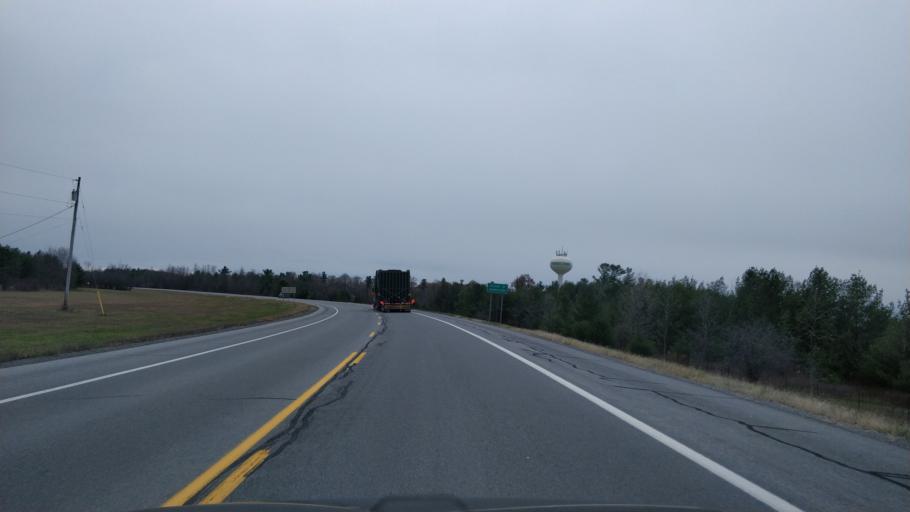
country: CA
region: Ontario
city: Brockville
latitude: 44.5915
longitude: -75.6398
